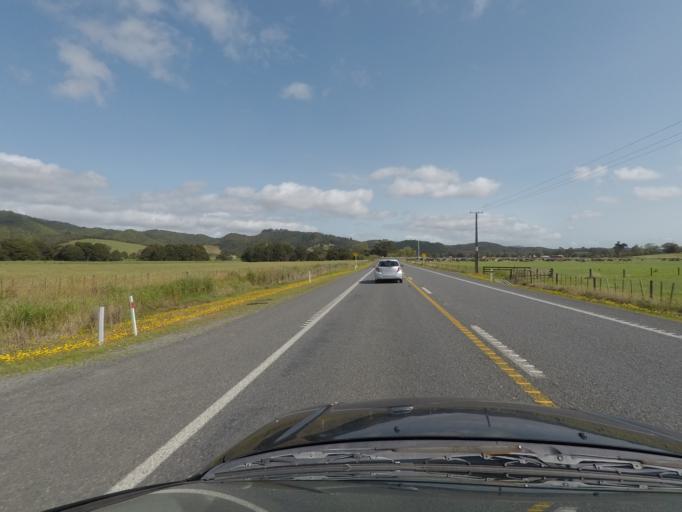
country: NZ
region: Northland
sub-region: Whangarei
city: Ruakaka
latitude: -36.0056
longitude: 174.4155
